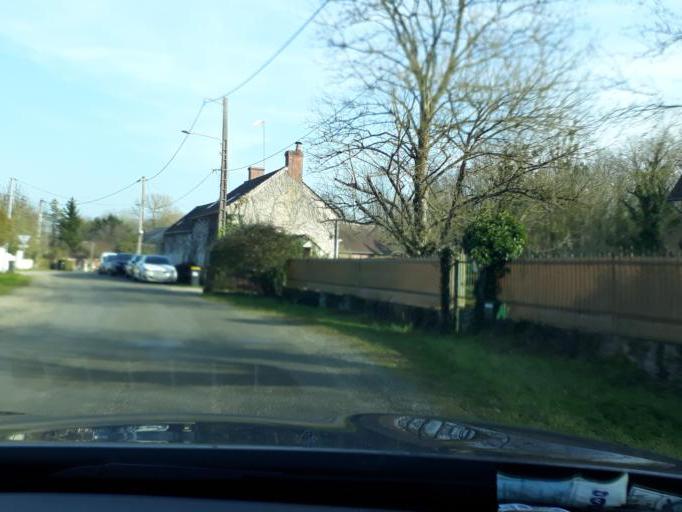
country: FR
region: Centre
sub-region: Departement du Loiret
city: Meung-sur-Loire
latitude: 47.8608
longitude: 1.6985
